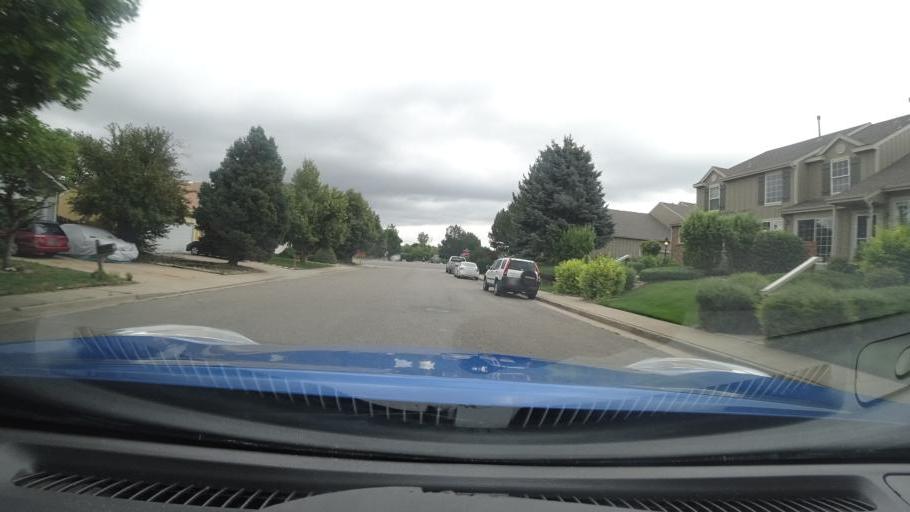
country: US
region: Colorado
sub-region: Adams County
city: Aurora
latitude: 39.7010
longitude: -104.8109
